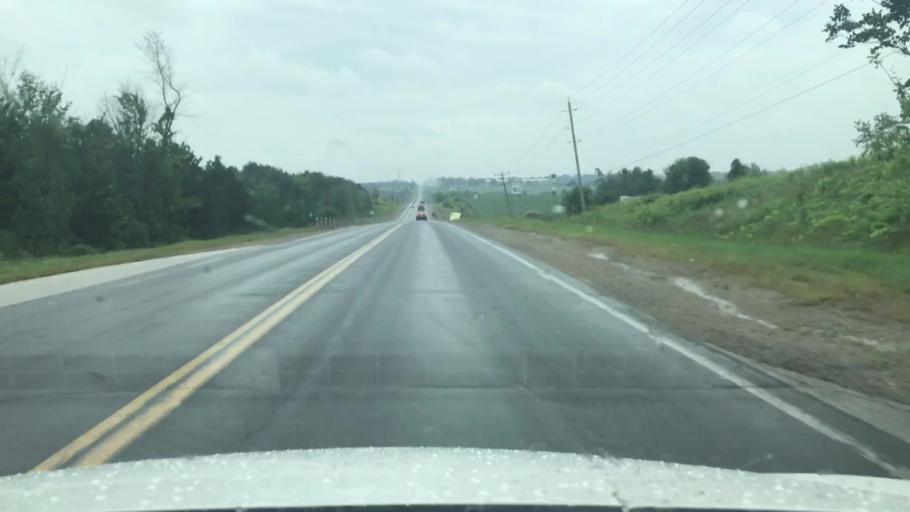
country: CA
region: Ontario
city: Bradford West Gwillimbury
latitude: 44.1630
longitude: -79.5768
